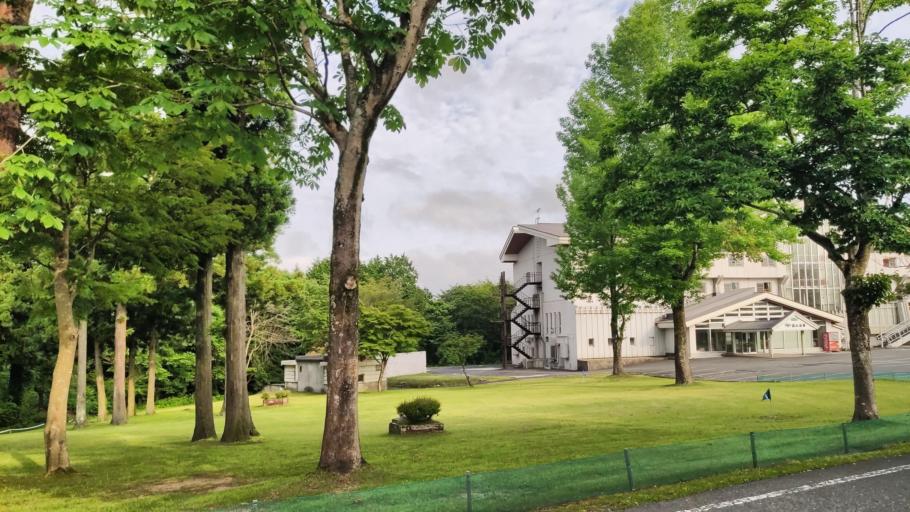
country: JP
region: Tottori
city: Kurayoshi
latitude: 35.2944
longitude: 133.6309
